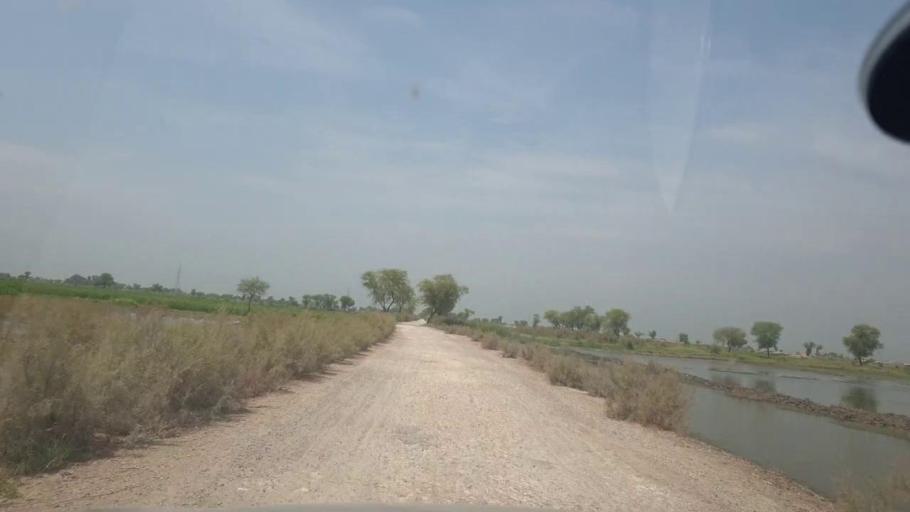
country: PK
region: Sindh
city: Thul
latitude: 28.1778
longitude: 68.6211
